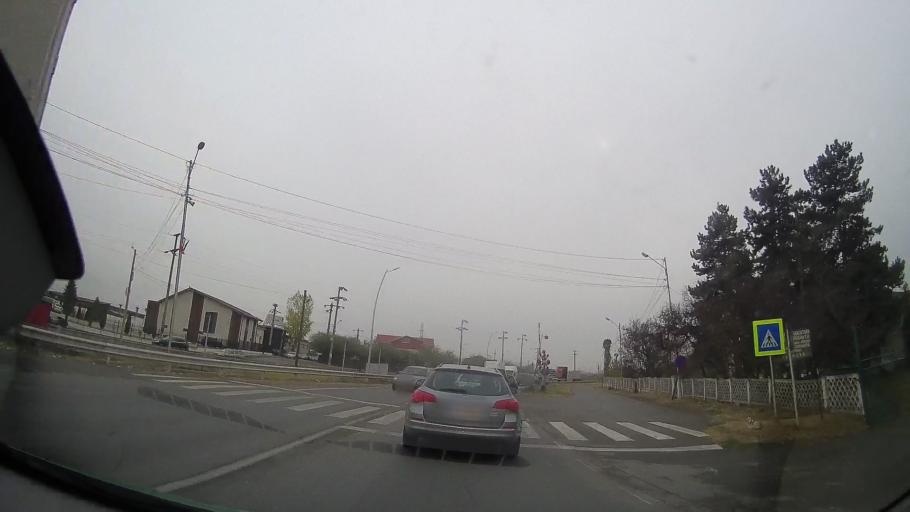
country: RO
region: Prahova
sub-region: Comuna Blejoiu
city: Ploiestiori
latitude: 44.9852
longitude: 26.0154
